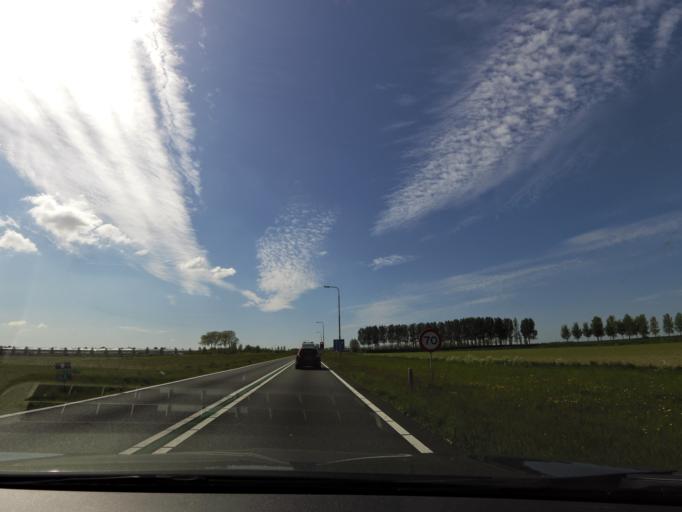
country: NL
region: South Holland
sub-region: Gemeente Goeree-Overflakkee
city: Middelharnis
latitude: 51.6955
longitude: 4.2356
